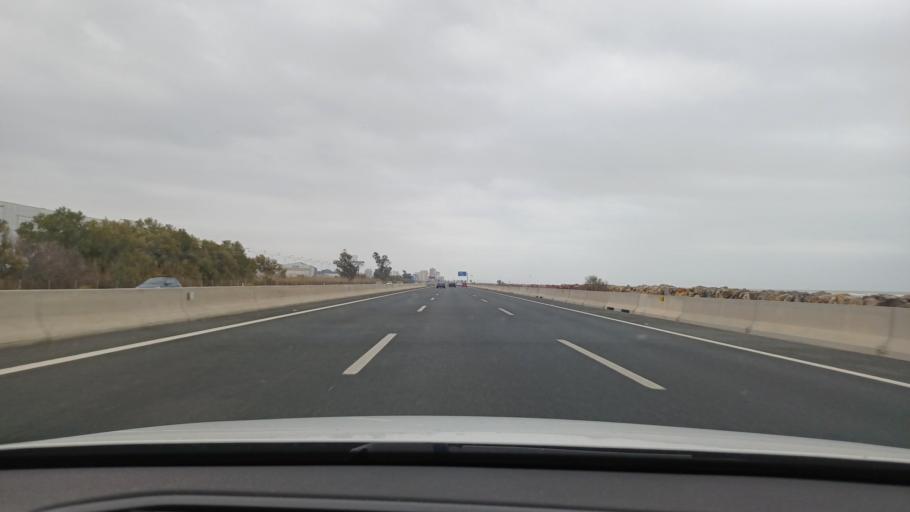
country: ES
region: Valencia
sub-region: Provincia de Valencia
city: Albuixech
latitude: 39.5407
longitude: -0.3038
